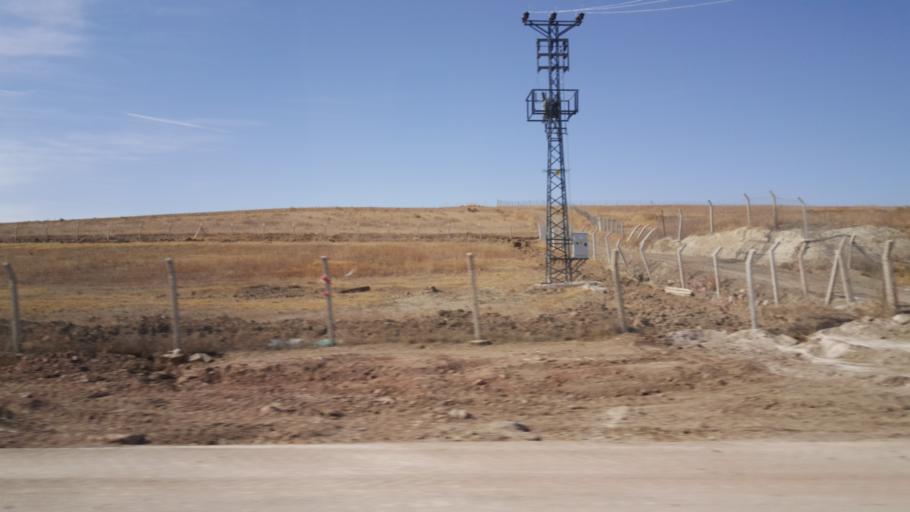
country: TR
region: Ankara
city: Ikizce
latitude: 39.6804
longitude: 32.7379
